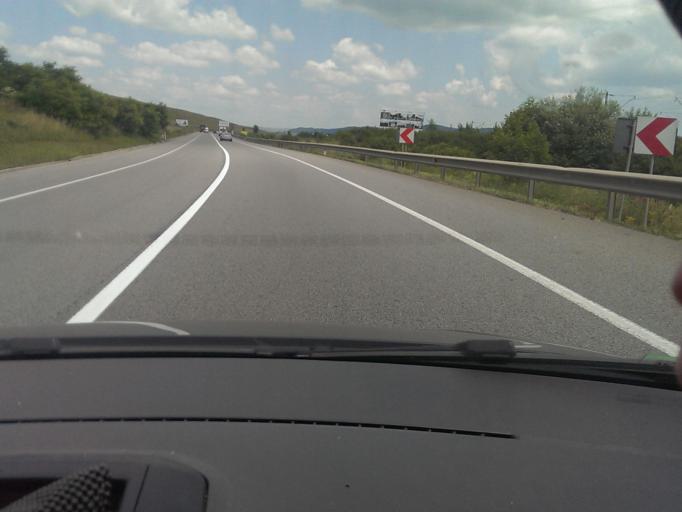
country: RO
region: Cluj
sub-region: Comuna Bontida
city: Rascruci
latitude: 46.8805
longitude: 23.7751
